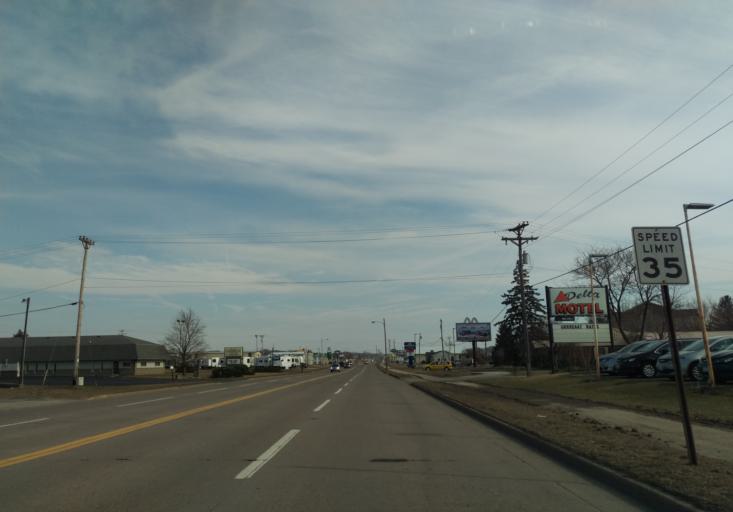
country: US
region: Wisconsin
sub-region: Crawford County
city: Prairie du Chien
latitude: 43.0312
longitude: -91.1322
